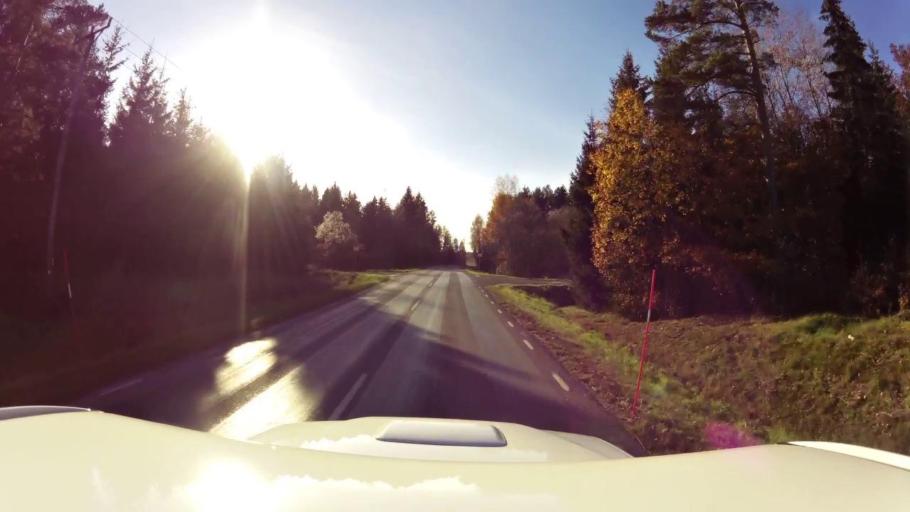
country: SE
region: OEstergoetland
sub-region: Linkopings Kommun
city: Vikingstad
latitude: 58.2939
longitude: 15.4631
